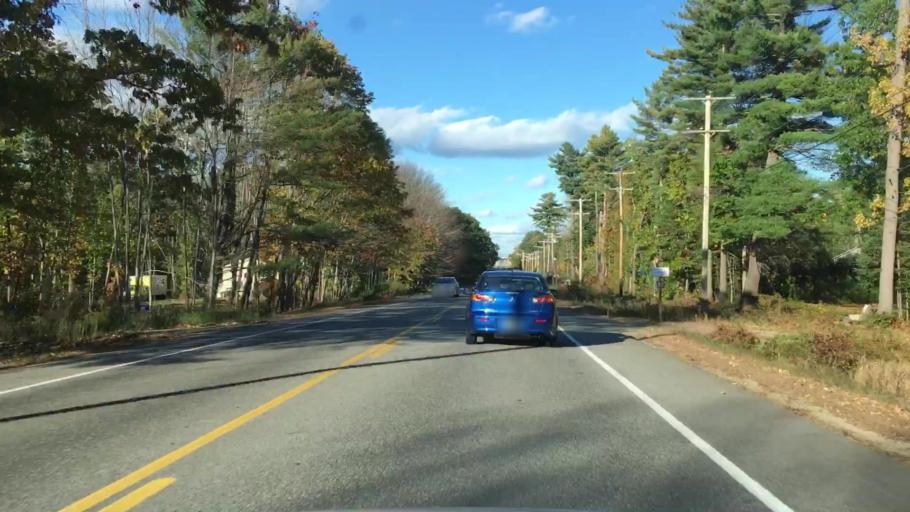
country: US
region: Maine
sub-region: Cumberland County
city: South Portland Gardens
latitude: 43.6132
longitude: -70.3576
